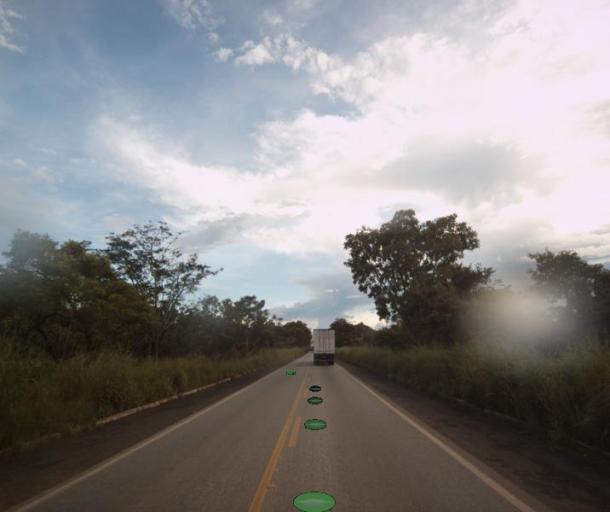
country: BR
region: Goias
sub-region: Uruacu
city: Uruacu
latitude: -14.0631
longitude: -49.0931
